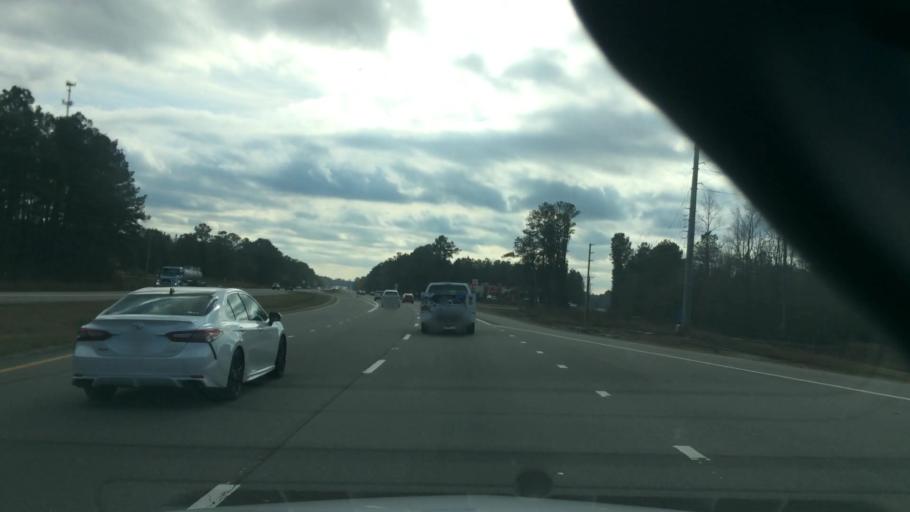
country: US
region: North Carolina
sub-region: Brunswick County
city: Leland
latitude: 34.1771
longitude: -78.0863
